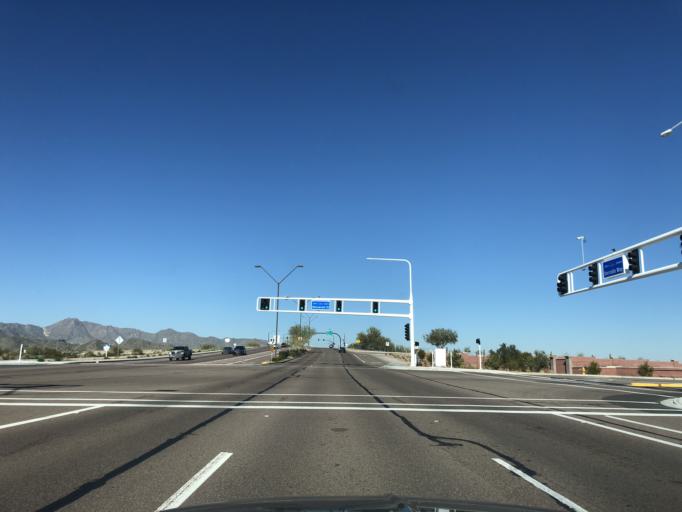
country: US
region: Arizona
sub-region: Maricopa County
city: Citrus Park
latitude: 33.4571
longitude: -112.5042
